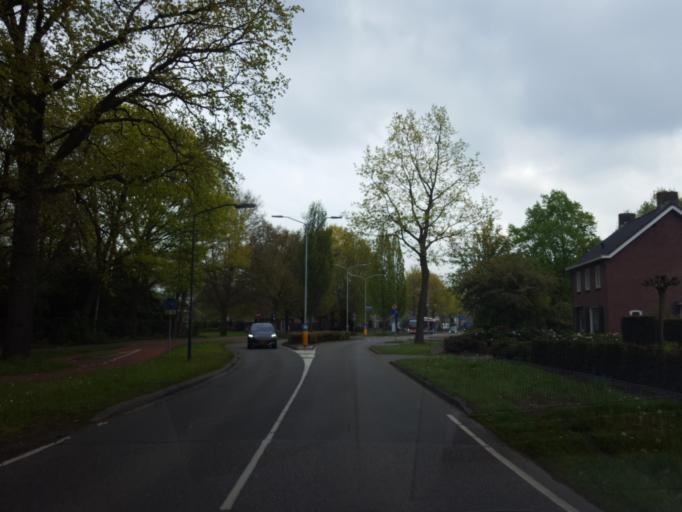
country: NL
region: North Brabant
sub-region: Gemeente Veldhoven
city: Oerle
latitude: 51.4137
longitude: 5.3839
